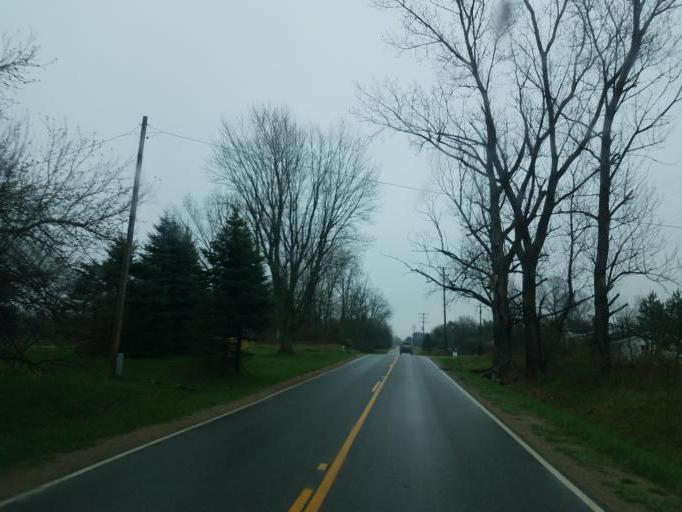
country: US
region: Michigan
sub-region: Isabella County
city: Lake Isabella
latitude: 43.5240
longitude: -84.9970
